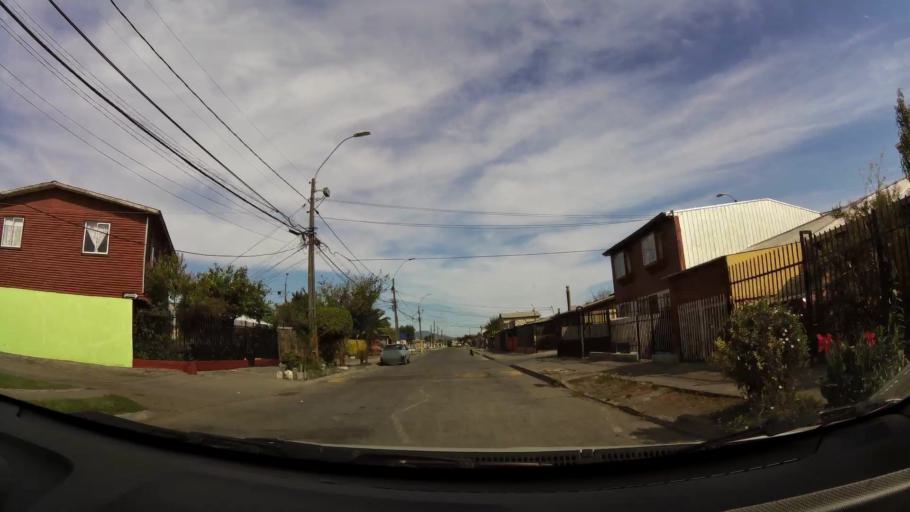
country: CL
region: Biobio
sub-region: Provincia de Concepcion
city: Talcahuano
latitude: -36.7786
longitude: -73.1063
